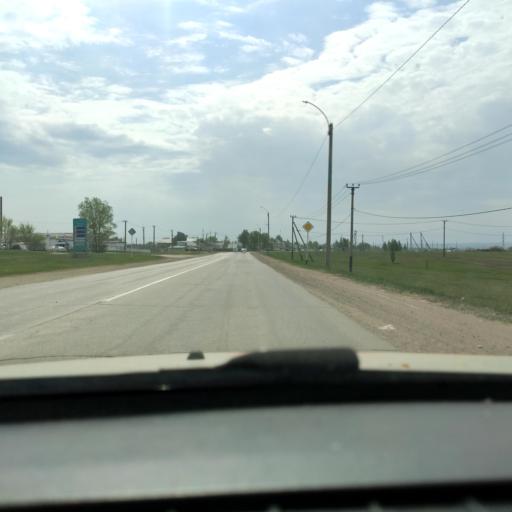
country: RU
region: Samara
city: Krasnyy Yar
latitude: 53.4834
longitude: 50.3909
